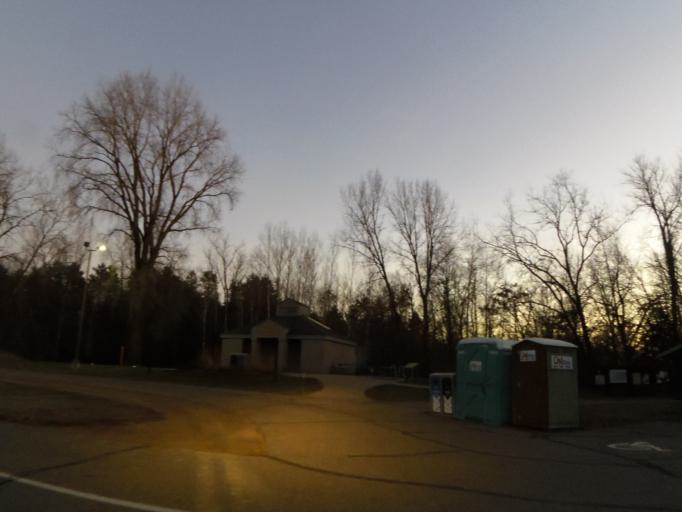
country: US
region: Minnesota
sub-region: Washington County
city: Stillwater
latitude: 45.1208
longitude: -92.8380
